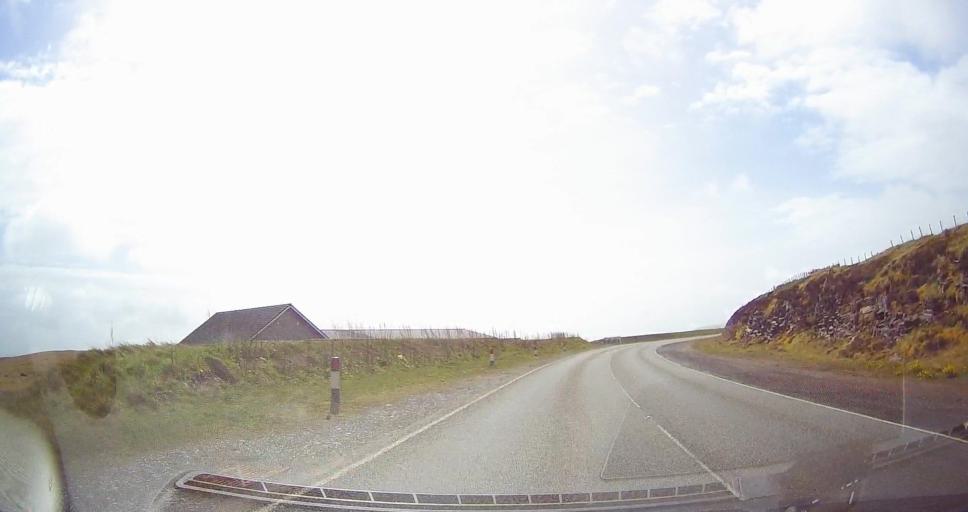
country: GB
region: Scotland
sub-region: Shetland Islands
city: Lerwick
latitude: 60.1213
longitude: -1.2154
